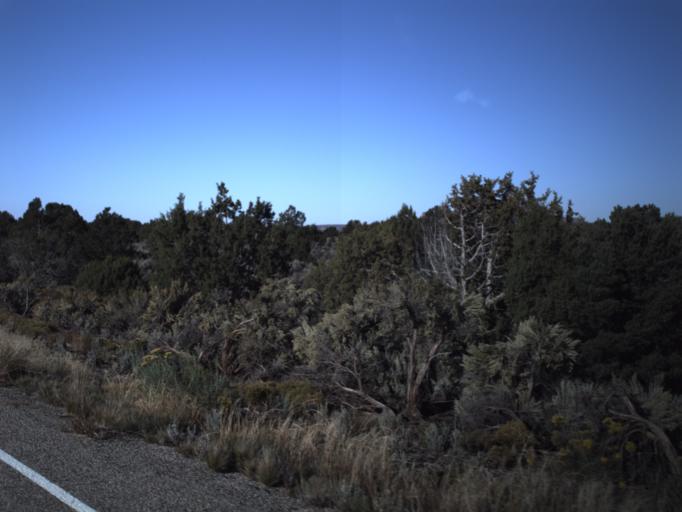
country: US
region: Utah
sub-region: San Juan County
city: Blanding
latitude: 37.5479
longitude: -109.9428
